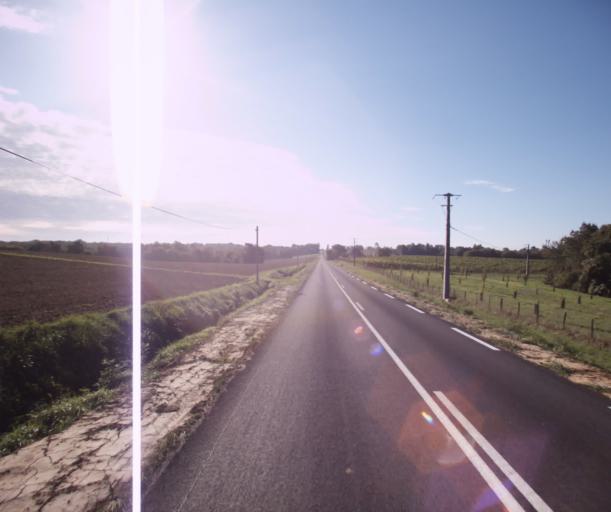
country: FR
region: Midi-Pyrenees
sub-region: Departement du Gers
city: Cazaubon
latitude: 43.9003
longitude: -0.0145
